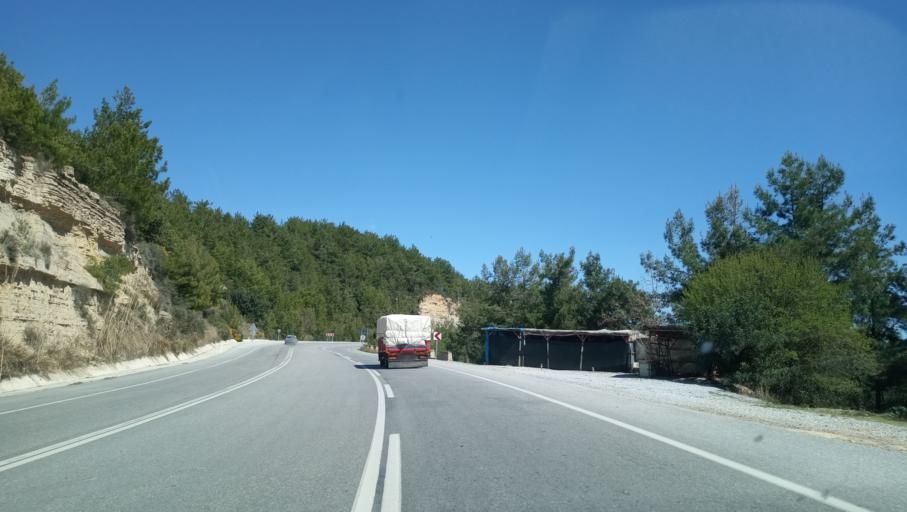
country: TR
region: Antalya
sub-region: Manavgat
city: Kizilagac
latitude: 36.7643
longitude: 31.6551
